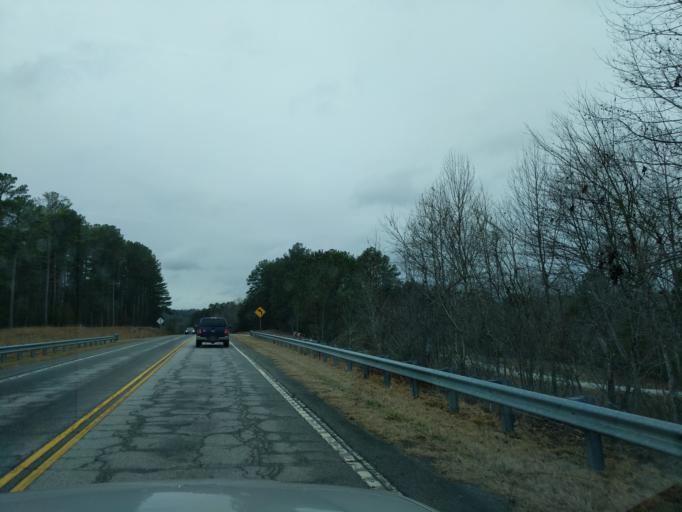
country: US
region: South Carolina
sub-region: Oconee County
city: Walhalla
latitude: 34.8454
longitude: -83.0347
